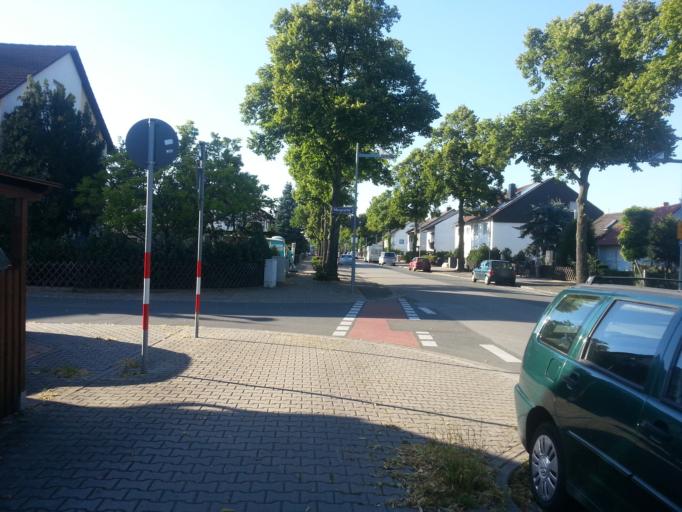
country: DE
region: Baden-Wuerttemberg
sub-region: Karlsruhe Region
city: Mannheim
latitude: 49.5215
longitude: 8.5125
